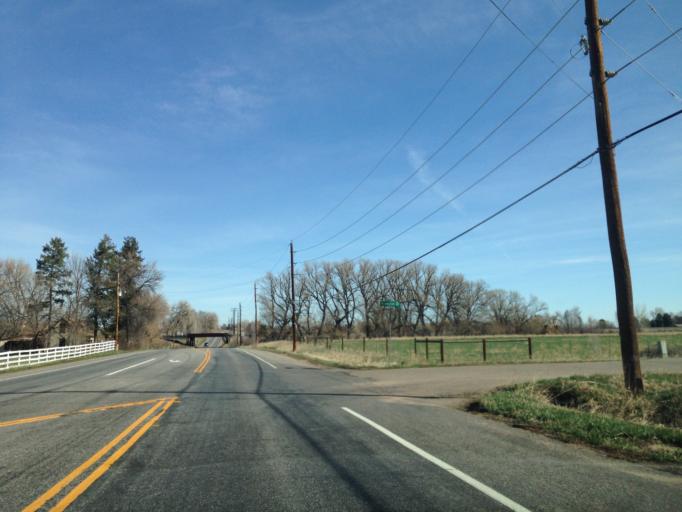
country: US
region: Colorado
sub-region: Boulder County
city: Louisville
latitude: 40.0068
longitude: -105.1782
